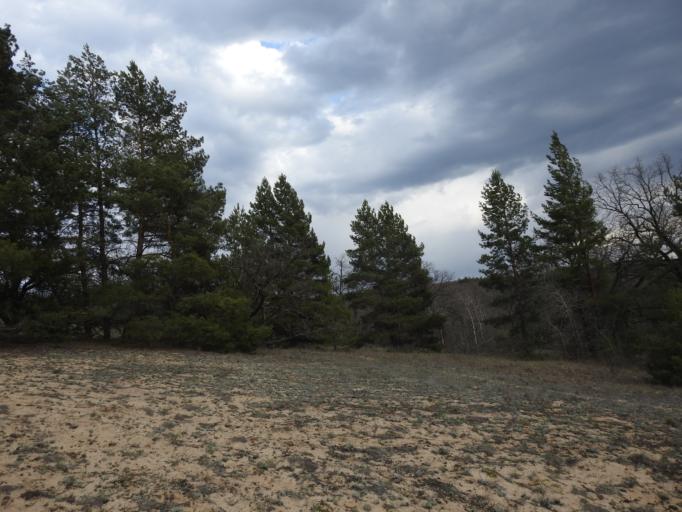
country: RU
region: Saratov
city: Krasnyy Oktyabr'
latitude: 51.4263
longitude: 45.5429
